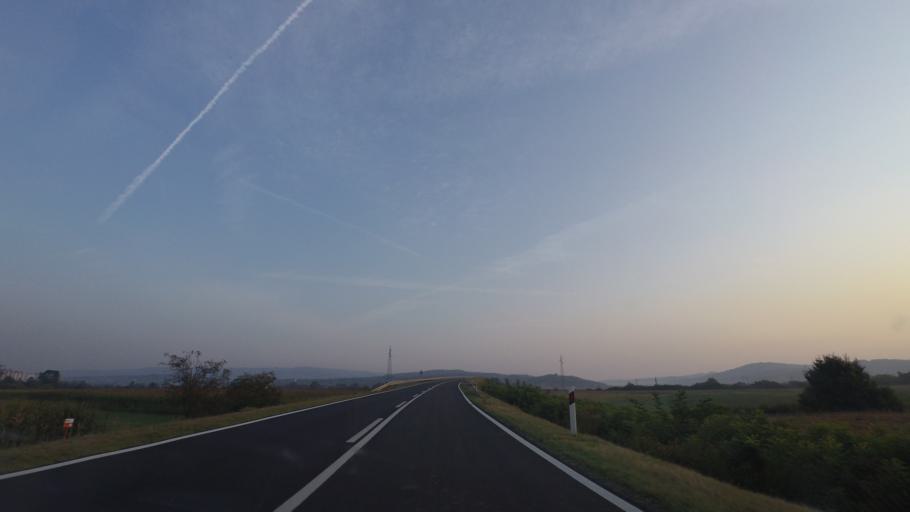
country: HR
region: Brodsko-Posavska
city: Nova Gradiska
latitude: 45.2443
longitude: 17.4083
